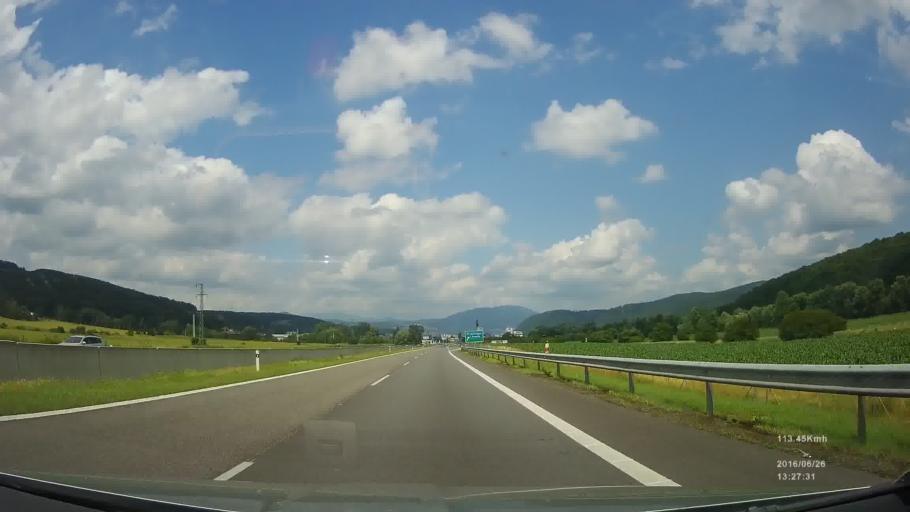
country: SK
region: Banskobystricky
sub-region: Okres Banska Bystrica
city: Banska Bystrica
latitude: 48.6846
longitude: 19.1320
